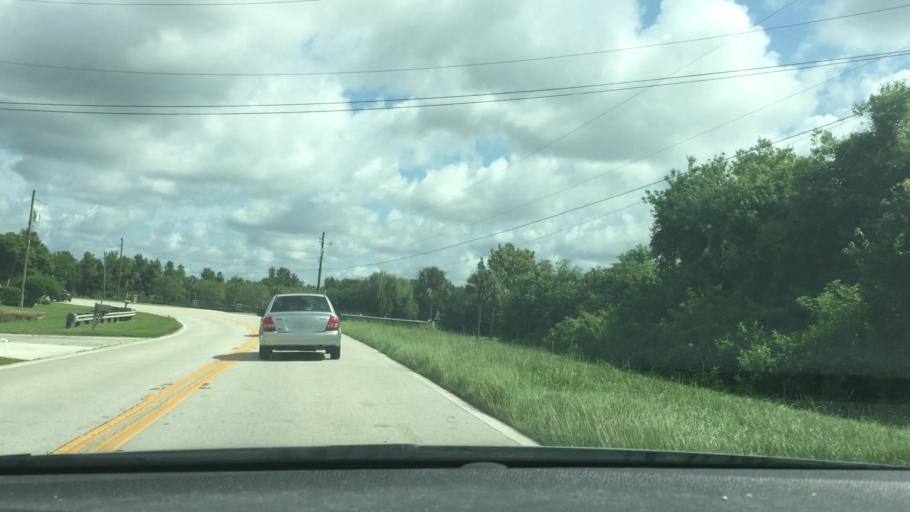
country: US
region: Florida
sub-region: Osceola County
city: Buenaventura Lakes
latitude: 28.3015
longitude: -81.3221
